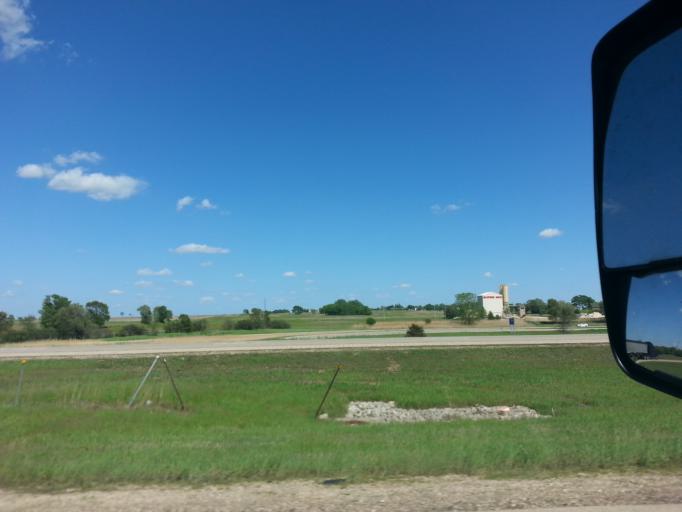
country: US
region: Illinois
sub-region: Ogle County
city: Davis Junction
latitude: 42.1033
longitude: -89.0230
